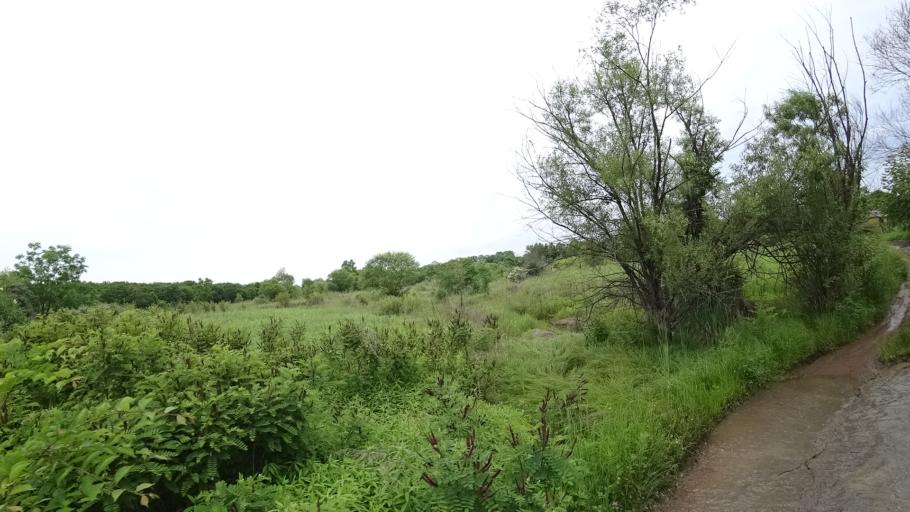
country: RU
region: Primorskiy
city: Novosysoyevka
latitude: 44.2110
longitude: 133.3268
